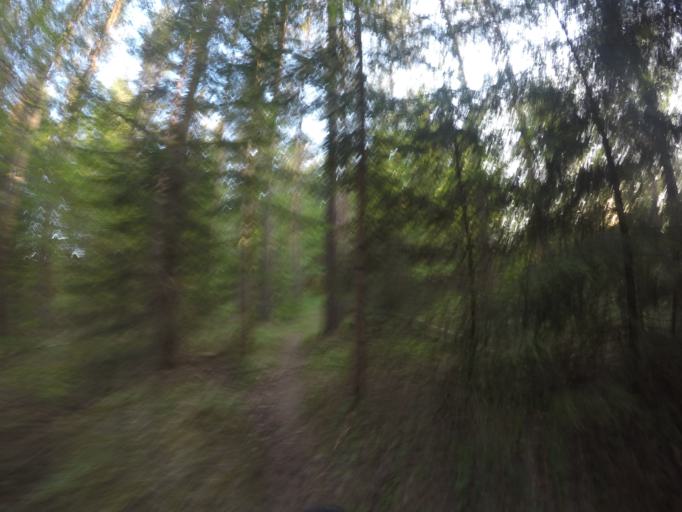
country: SE
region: Soedermanland
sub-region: Eskilstuna Kommun
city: Eskilstuna
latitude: 59.3307
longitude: 16.5246
